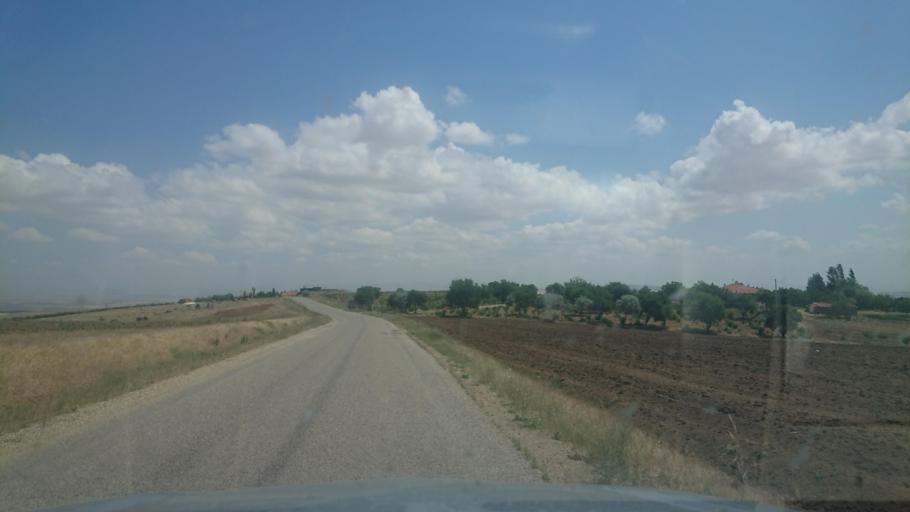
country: TR
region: Aksaray
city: Agacoren
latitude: 38.8703
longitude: 33.9396
